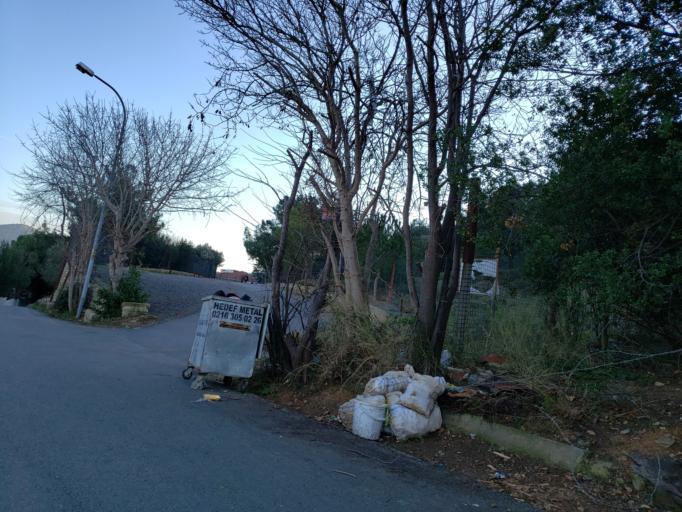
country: TR
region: Istanbul
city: Adalan
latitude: 40.8829
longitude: 29.0986
